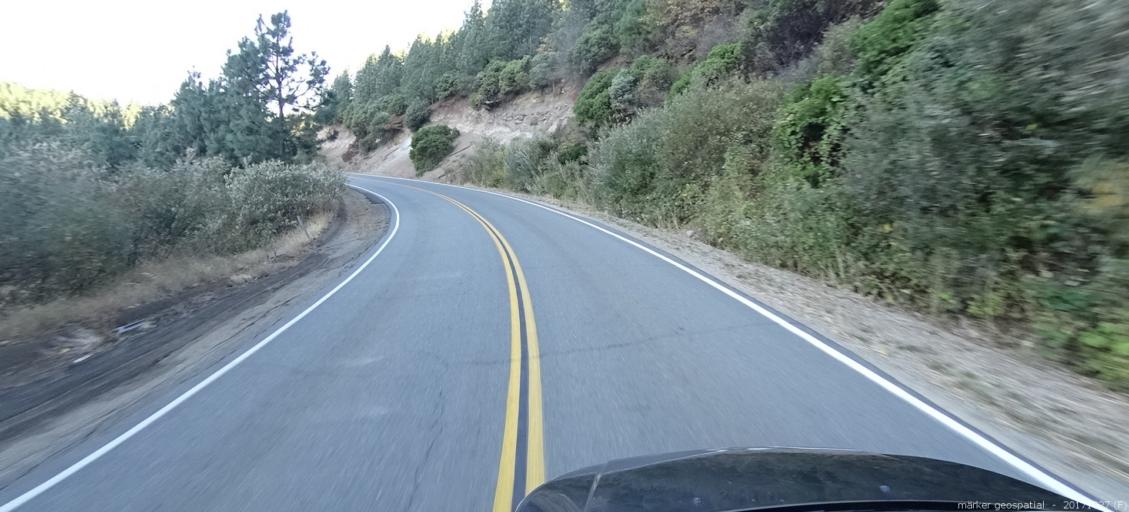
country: US
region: California
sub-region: Shasta County
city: Burney
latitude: 40.8728
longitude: -121.9004
